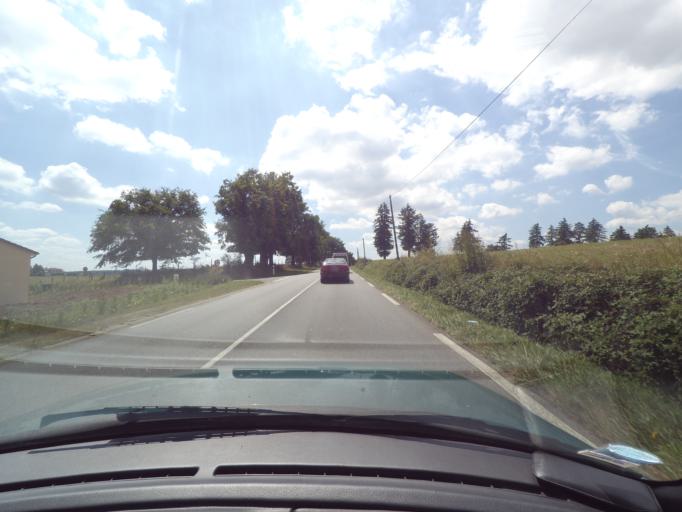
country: FR
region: Limousin
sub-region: Departement de la Haute-Vienne
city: Limoges
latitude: 45.7995
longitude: 1.2526
